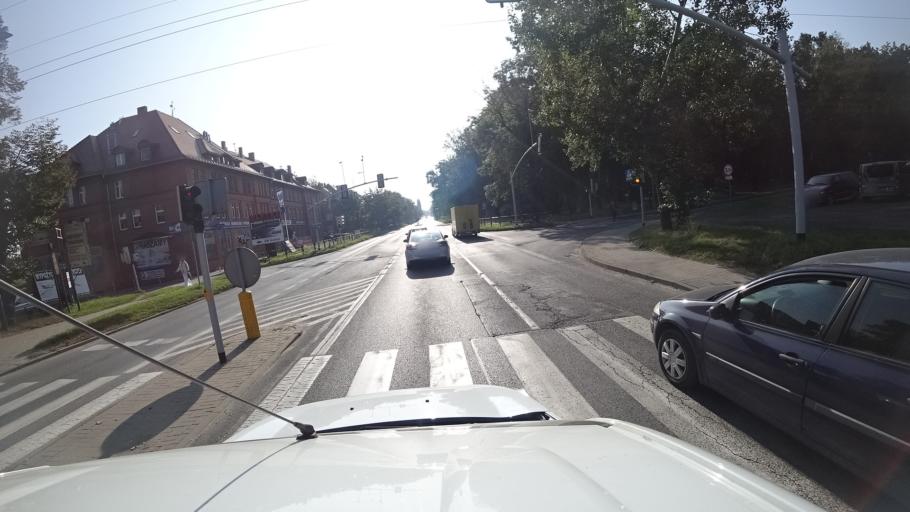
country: PL
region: Silesian Voivodeship
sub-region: Gliwice
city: Gliwice
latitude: 50.2825
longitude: 18.6832
